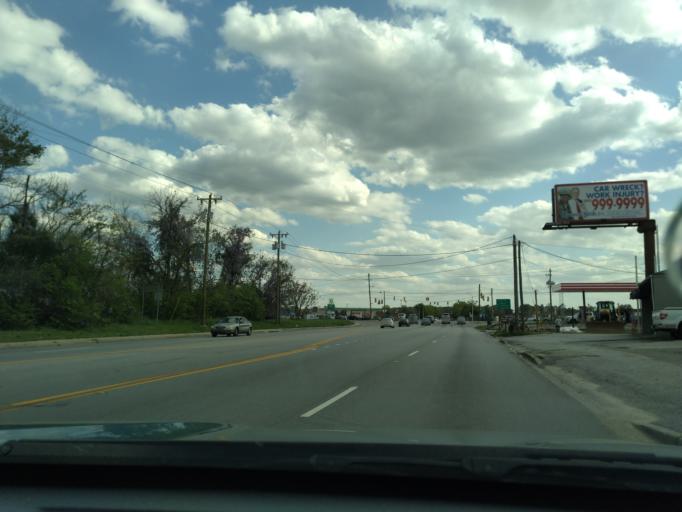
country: US
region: South Carolina
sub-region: Florence County
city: Florence
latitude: 34.1655
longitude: -79.7603
